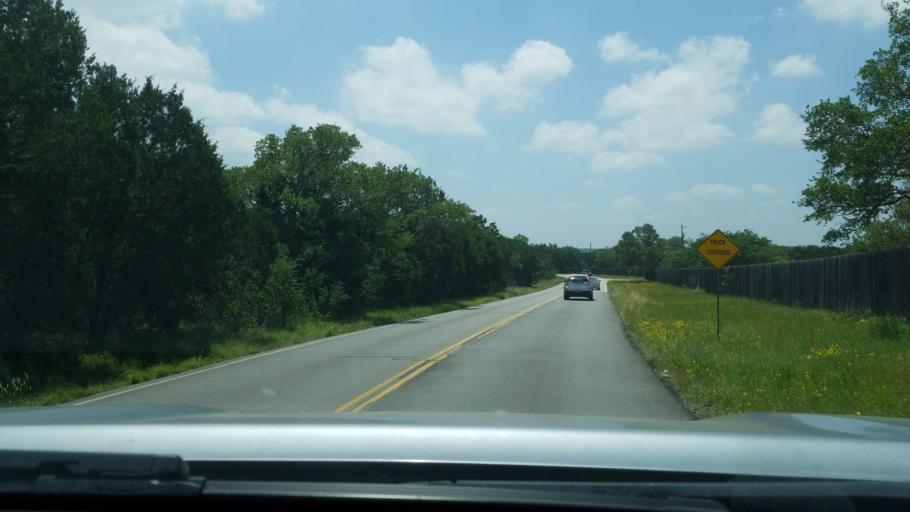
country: US
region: Texas
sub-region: Hays County
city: Woodcreek
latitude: 30.0392
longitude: -98.1135
